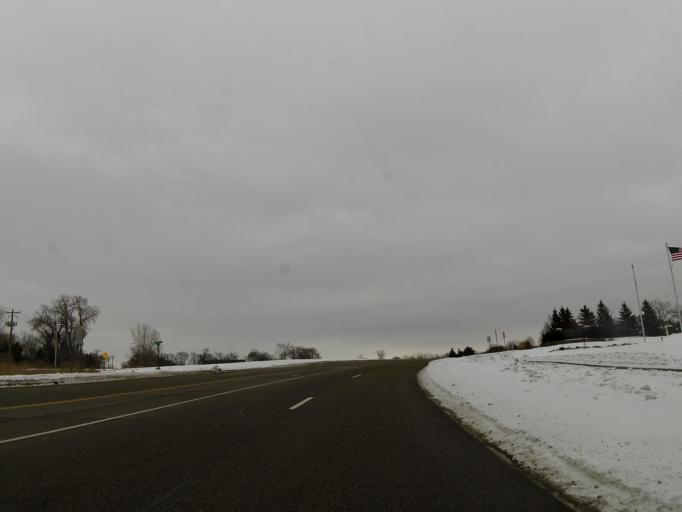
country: US
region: Minnesota
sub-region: Dakota County
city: Inver Grove Heights
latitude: 44.8478
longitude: -93.0693
